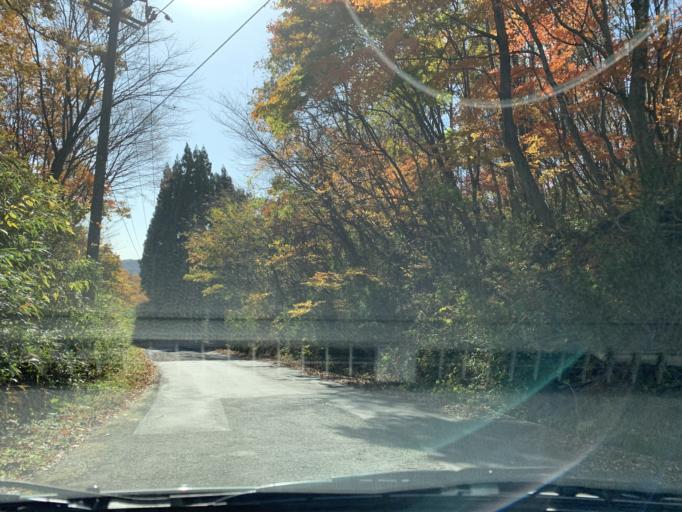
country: JP
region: Iwate
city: Ichinoseki
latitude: 39.0244
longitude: 141.0968
